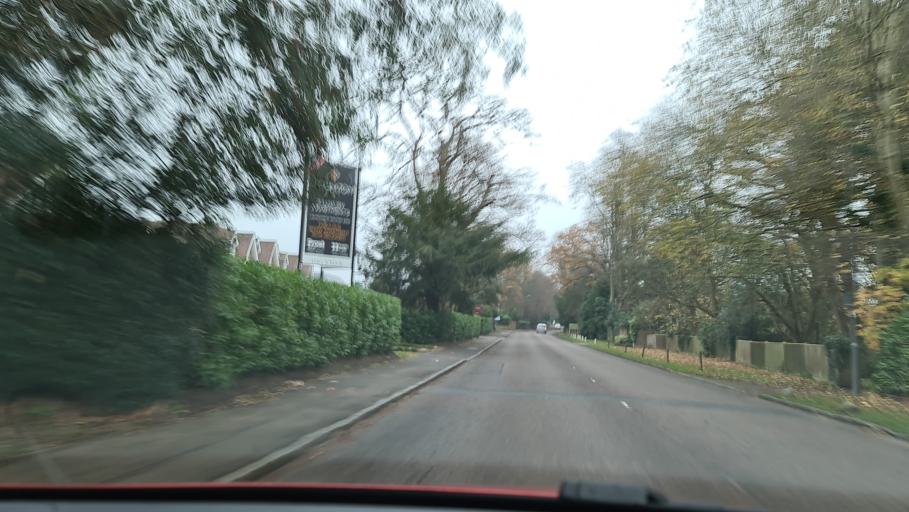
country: GB
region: England
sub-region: Buckinghamshire
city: Beaconsfield
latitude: 51.6196
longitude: -0.6504
